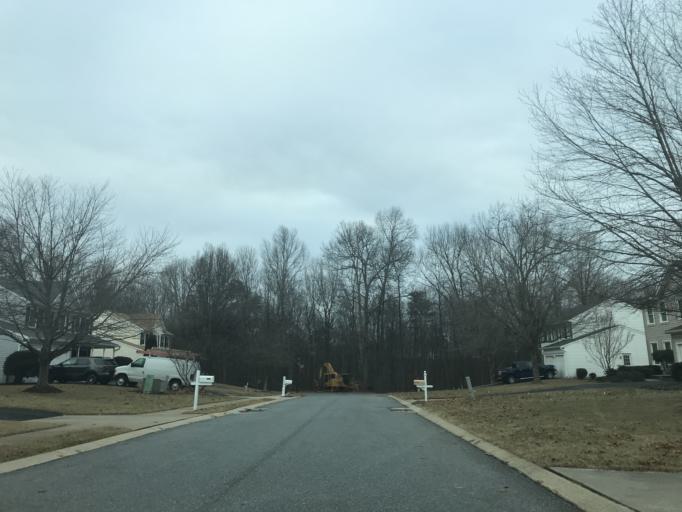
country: US
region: Maryland
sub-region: Carroll County
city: Eldersburg
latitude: 39.4087
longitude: -76.9235
